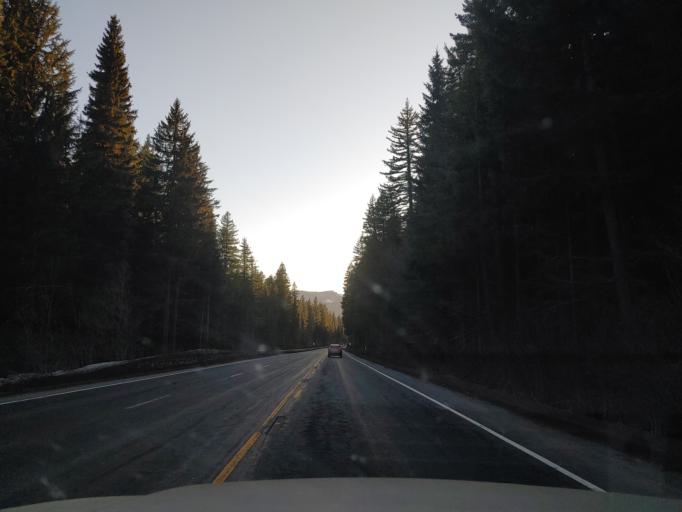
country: US
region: Oregon
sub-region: Lane County
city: Oakridge
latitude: 43.6196
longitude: -122.0747
